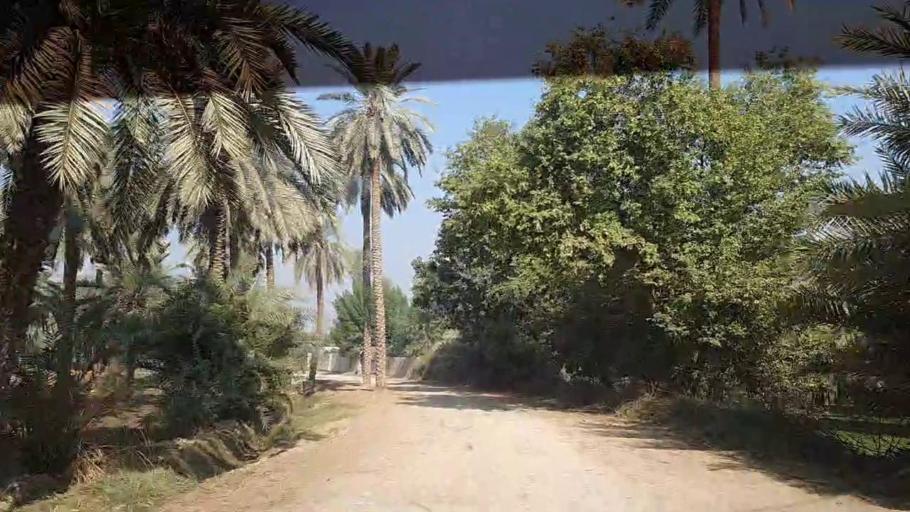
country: PK
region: Sindh
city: Khairpur
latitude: 27.4930
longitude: 68.7391
